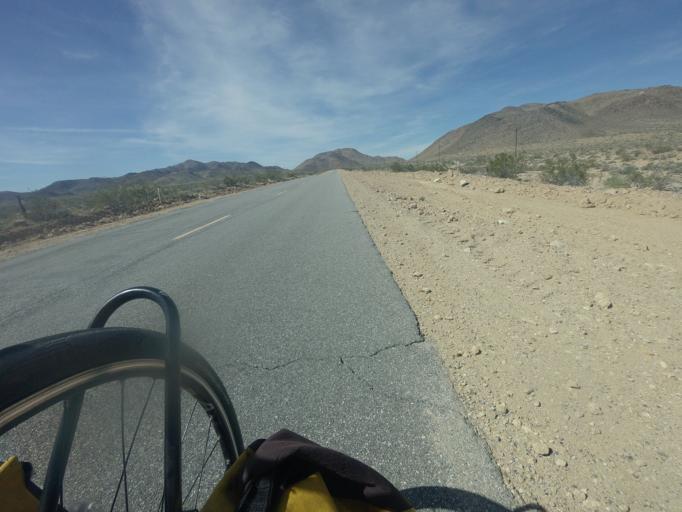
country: US
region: California
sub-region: San Bernardino County
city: Searles Valley
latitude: 35.5740
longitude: -117.4494
